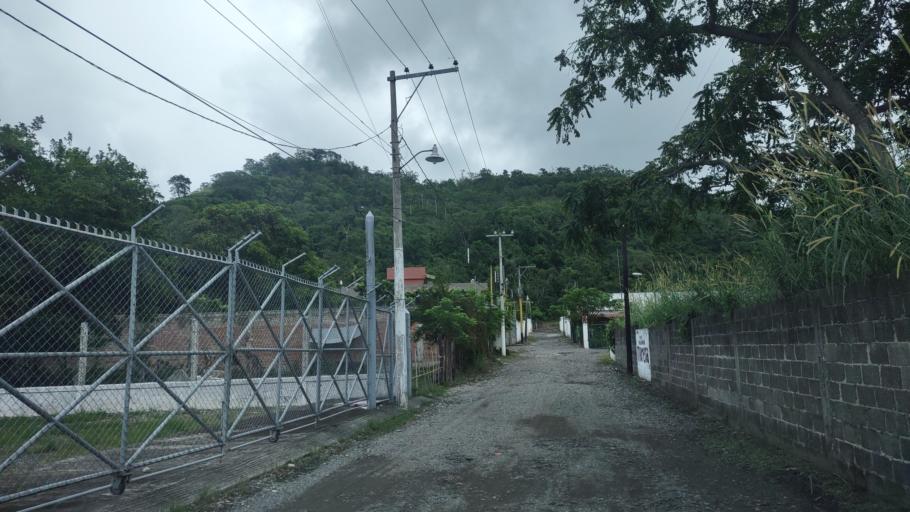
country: MX
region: Veracruz
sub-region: Papantla
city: Fraccionamiento la Florida
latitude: 20.5859
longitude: -97.4242
